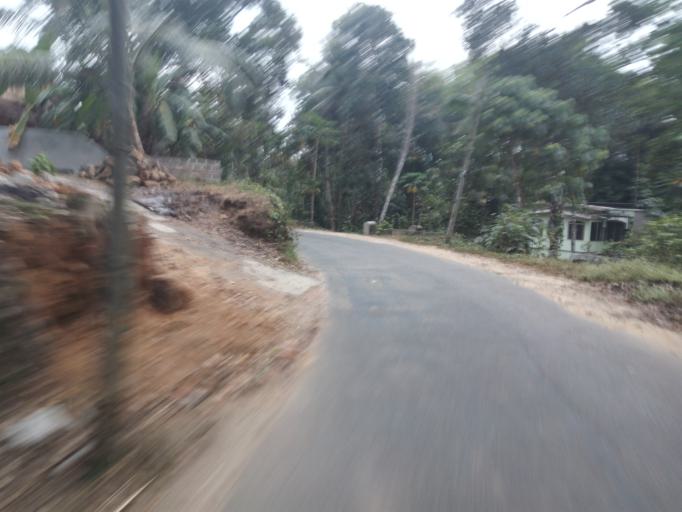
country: IN
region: Kerala
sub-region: Ernakulam
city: Muvattupuzha
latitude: 9.8800
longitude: 76.6467
